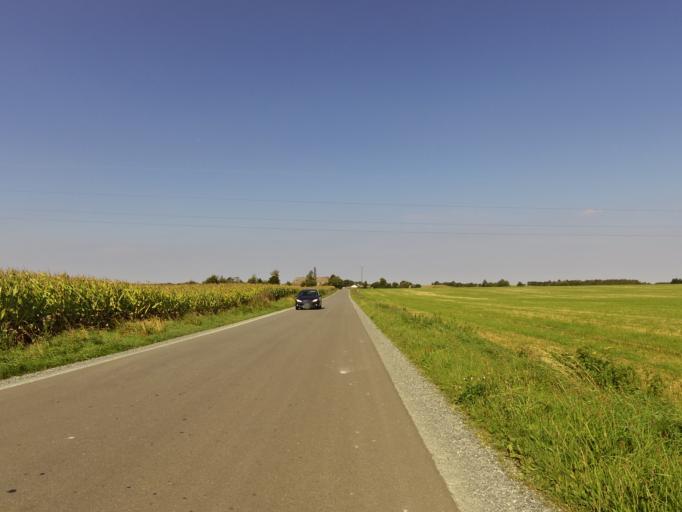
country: DK
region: South Denmark
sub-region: Vejen Kommune
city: Rodding
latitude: 55.3500
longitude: 9.1271
